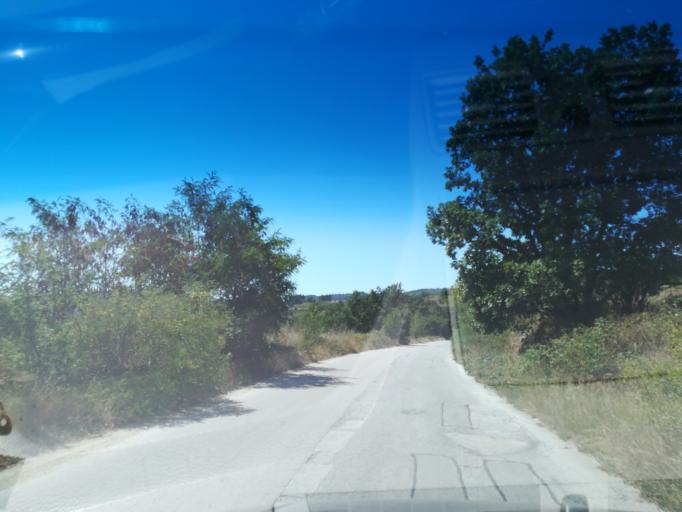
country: BG
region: Pazardzhik
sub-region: Obshtina Strelcha
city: Strelcha
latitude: 42.5241
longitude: 24.3246
